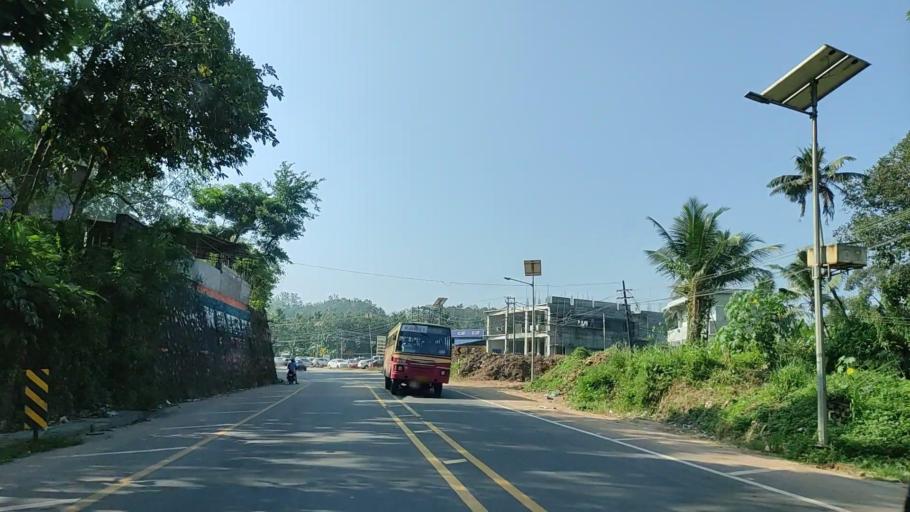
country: IN
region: Kerala
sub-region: Kollam
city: Punalur
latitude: 8.8792
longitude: 76.8669
